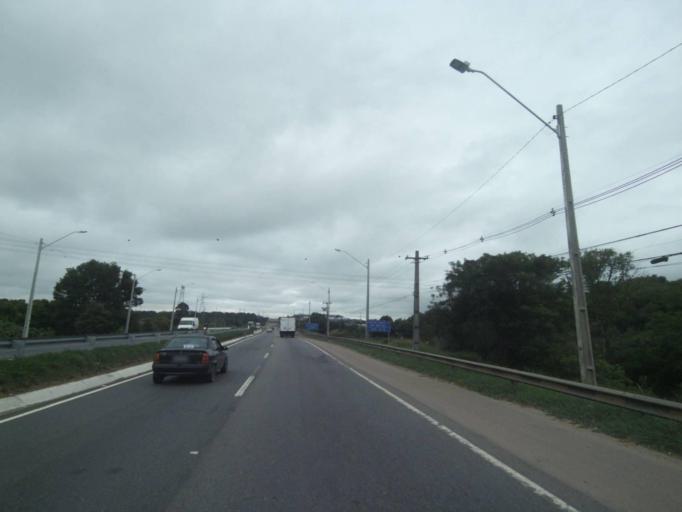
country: BR
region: Parana
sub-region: Araucaria
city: Araucaria
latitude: -25.5562
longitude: -49.3435
